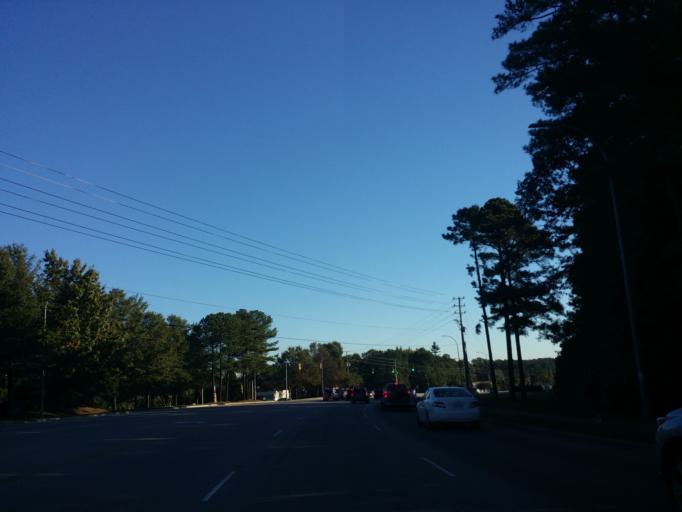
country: US
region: North Carolina
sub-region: Wake County
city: Cary
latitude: 35.8288
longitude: -78.7694
